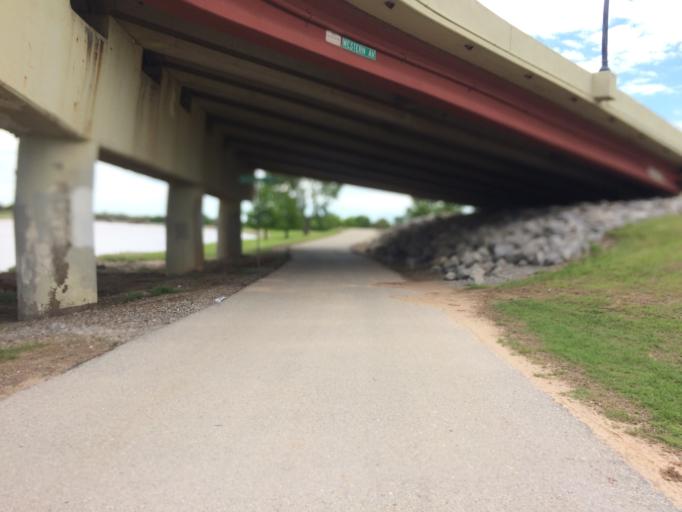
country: US
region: Oklahoma
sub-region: Oklahoma County
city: Oklahoma City
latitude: 35.4518
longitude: -97.5304
